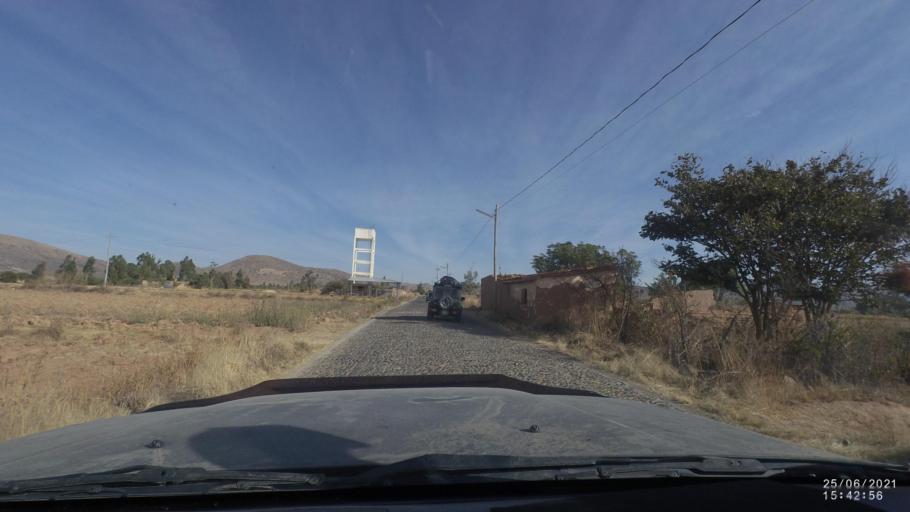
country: BO
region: Cochabamba
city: Cliza
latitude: -17.6435
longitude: -65.9117
